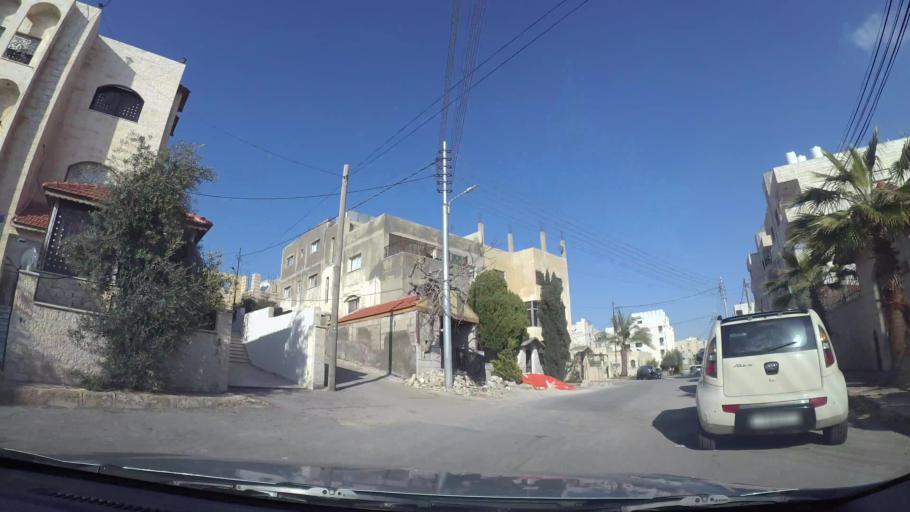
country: JO
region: Amman
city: Al Bunayyat ash Shamaliyah
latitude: 31.8978
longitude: 35.9158
